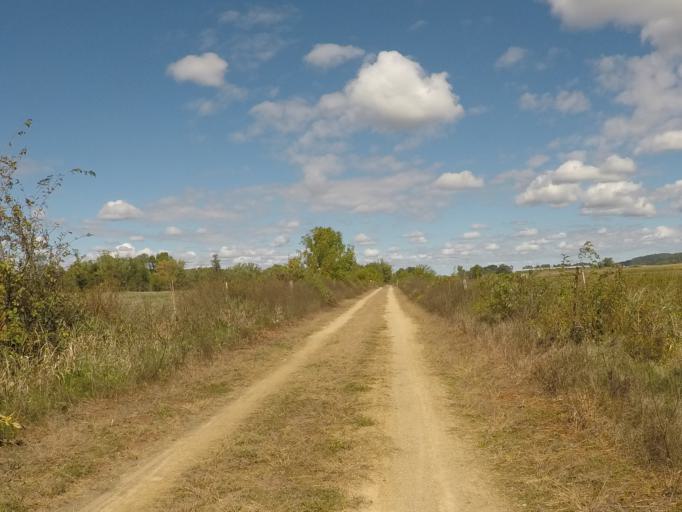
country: US
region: Wisconsin
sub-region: Richland County
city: Richland Center
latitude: 43.2342
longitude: -90.3000
